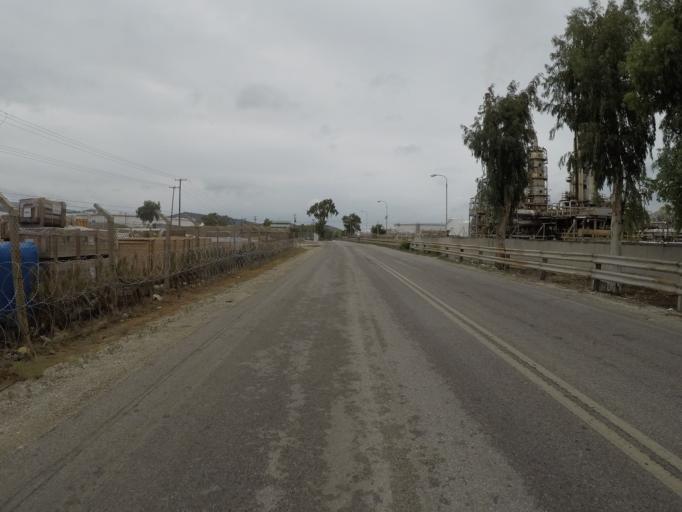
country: GR
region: Peloponnese
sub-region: Nomos Korinthias
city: Agioi Theodoroi
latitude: 37.9197
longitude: 23.0733
